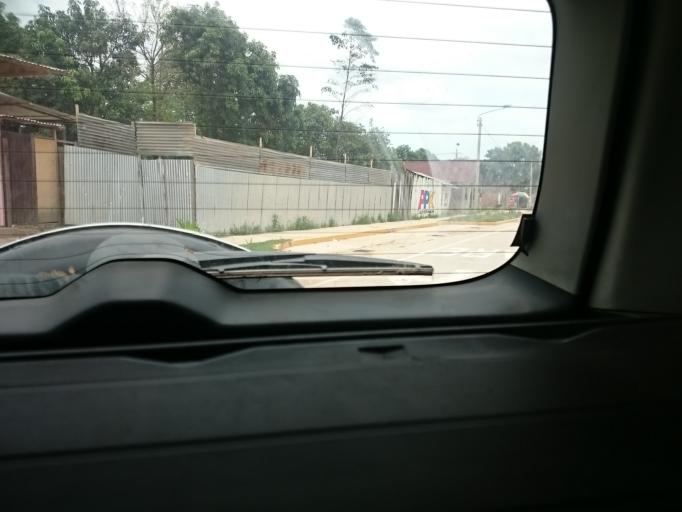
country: PE
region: Ucayali
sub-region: Provincia de Coronel Portillo
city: Pucallpa
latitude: -8.4165
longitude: -74.5581
